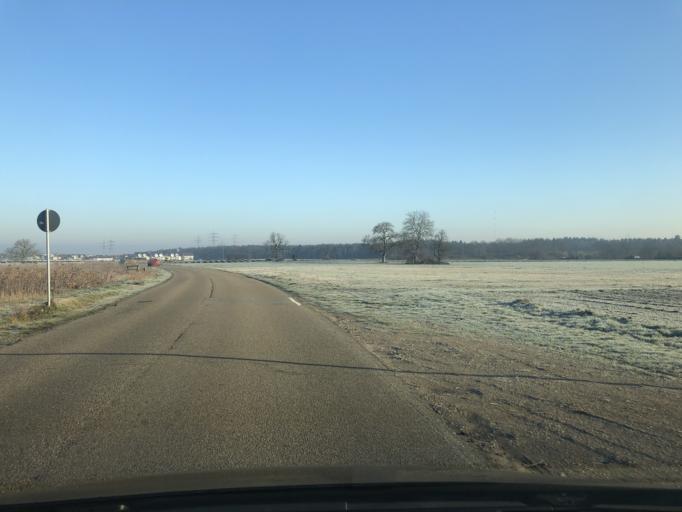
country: DE
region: Baden-Wuerttemberg
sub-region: Karlsruhe Region
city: Eggenstein-Leopoldshafen
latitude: 49.0752
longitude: 8.4026
